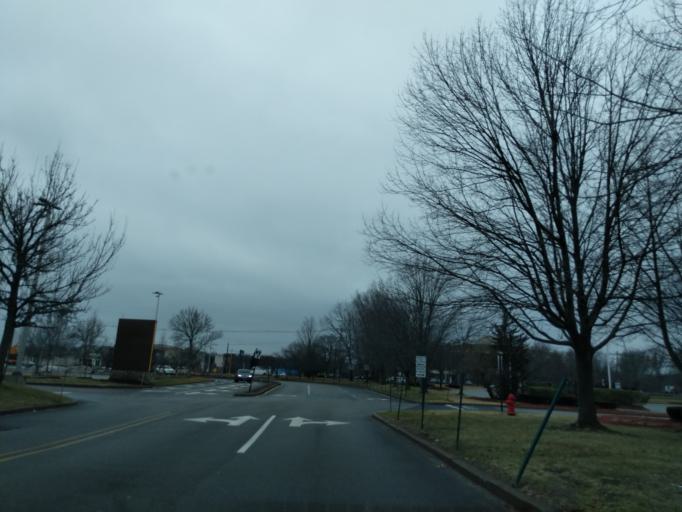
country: US
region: Massachusetts
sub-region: Middlesex County
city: Cochituate
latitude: 42.3004
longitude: -71.3882
